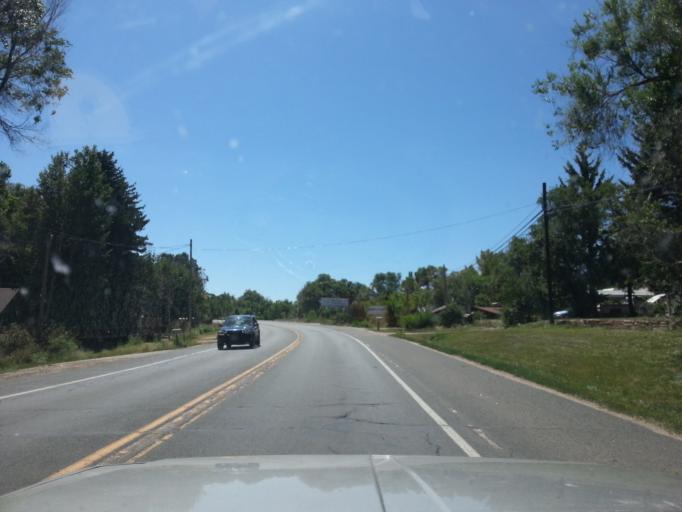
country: US
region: Colorado
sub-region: Larimer County
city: Loveland
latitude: 40.4129
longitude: -105.1688
